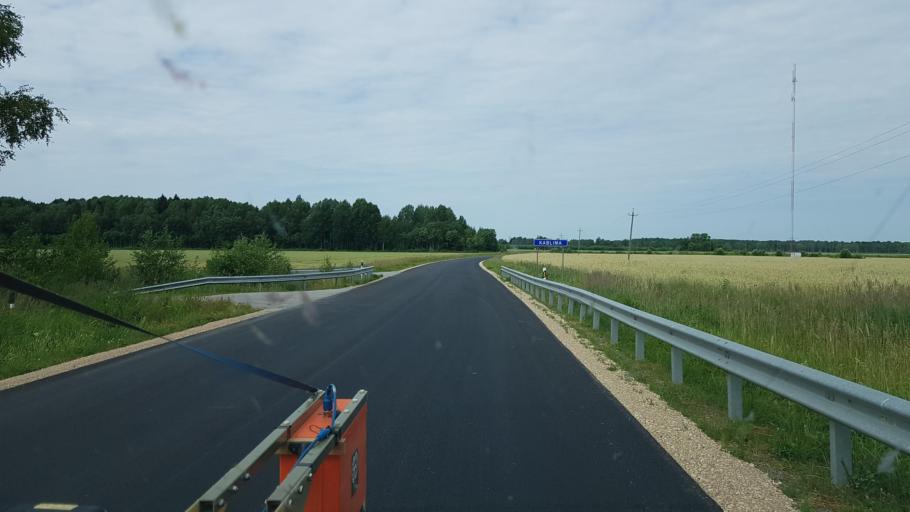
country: EE
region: Paernumaa
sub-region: Halinga vald
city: Parnu-Jaagupi
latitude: 58.6241
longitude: 24.3737
